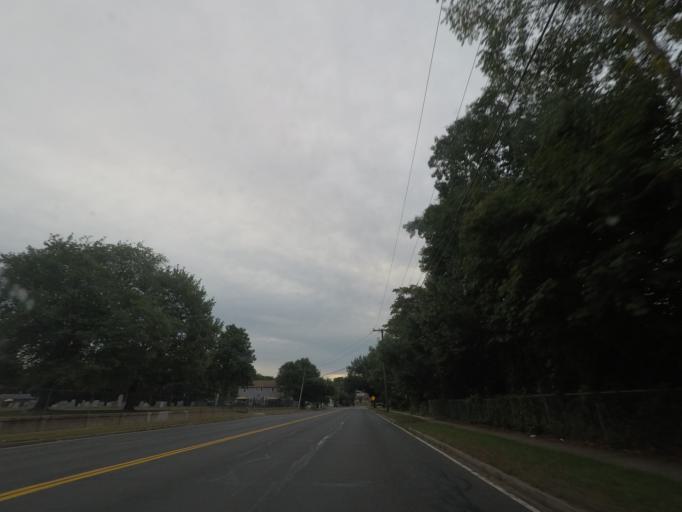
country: US
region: Massachusetts
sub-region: Hampden County
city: Ludlow
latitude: 42.1490
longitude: -72.5130
